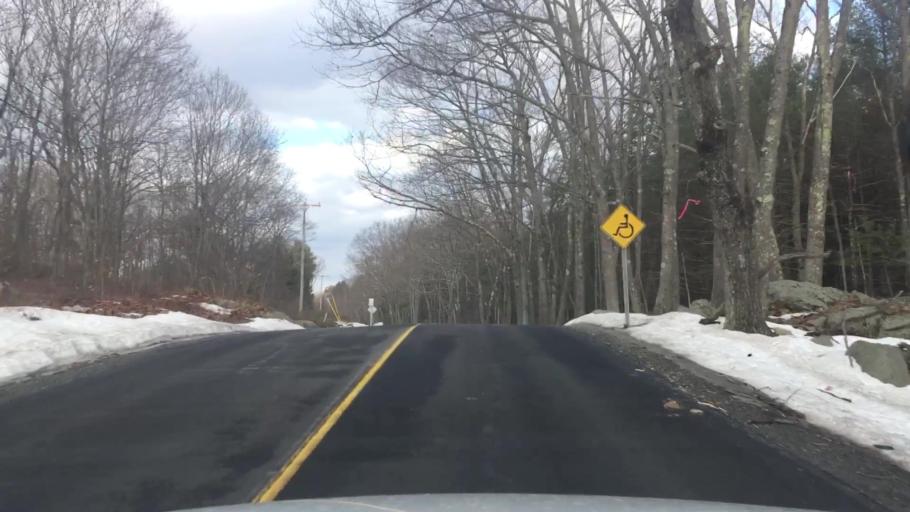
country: US
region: Maine
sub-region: York County
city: Arundel
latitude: 43.4193
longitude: -70.4627
